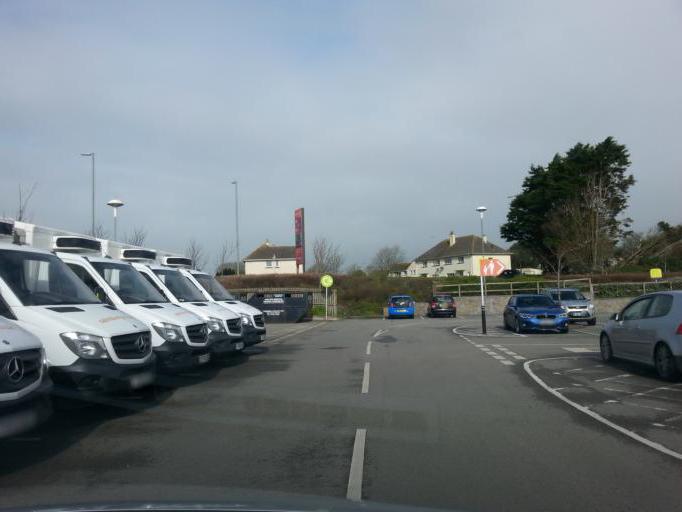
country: GB
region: England
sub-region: Cornwall
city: Helston
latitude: 50.0925
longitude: -5.2621
